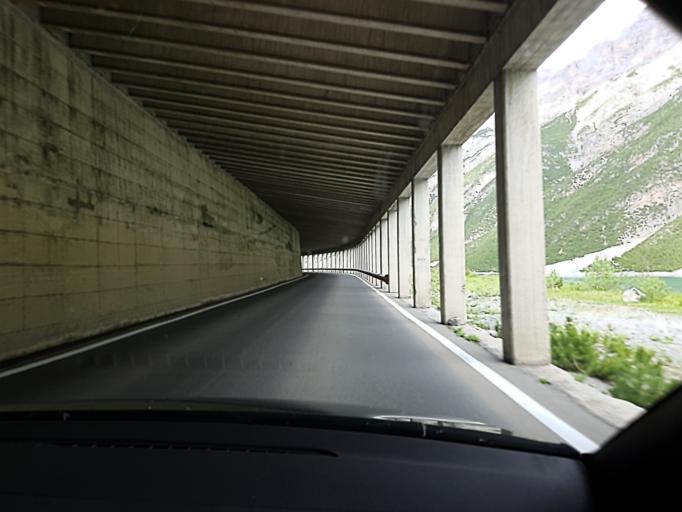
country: IT
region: Lombardy
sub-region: Provincia di Sondrio
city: Livigno
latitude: 46.5728
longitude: 10.1637
